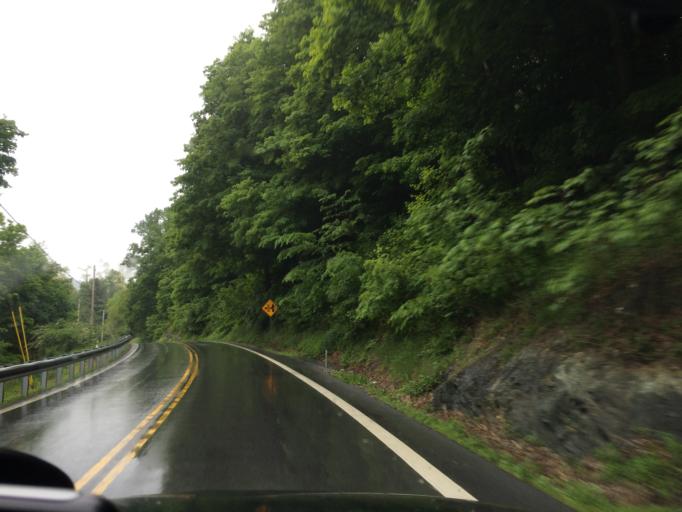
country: US
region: Maryland
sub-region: Washington County
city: Highfield-Cascade
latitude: 39.6726
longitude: -77.4539
